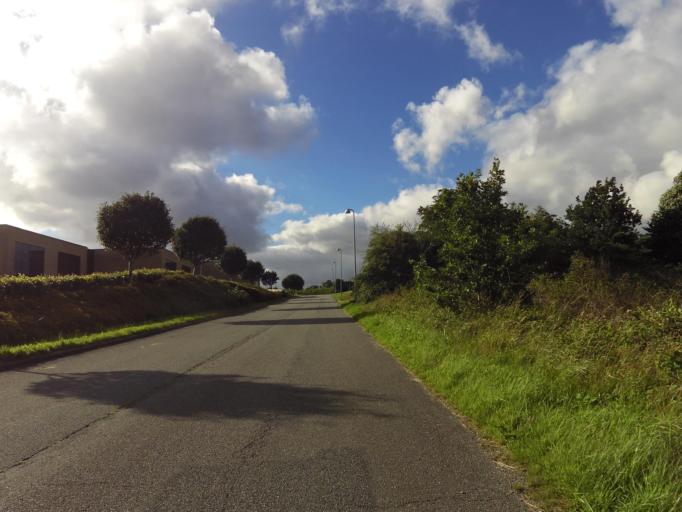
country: DK
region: South Denmark
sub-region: Tonder Kommune
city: Toftlund
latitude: 55.1791
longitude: 9.0674
